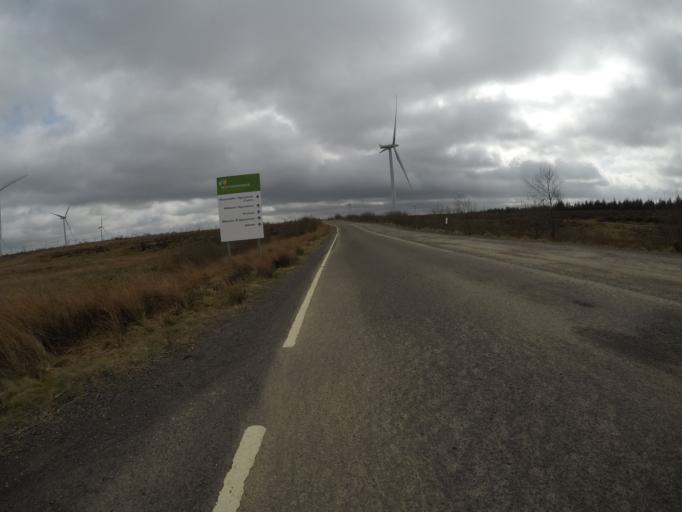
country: GB
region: Scotland
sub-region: East Renfrewshire
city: Newton Mearns
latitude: 55.7051
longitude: -4.3573
